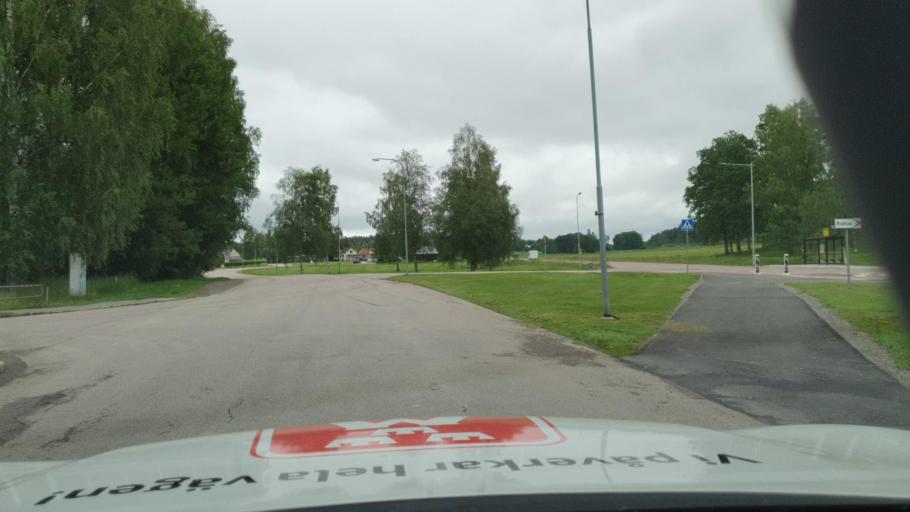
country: SE
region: Vaermland
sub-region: Grums Kommun
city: Grums
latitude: 59.3652
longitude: 13.1149
